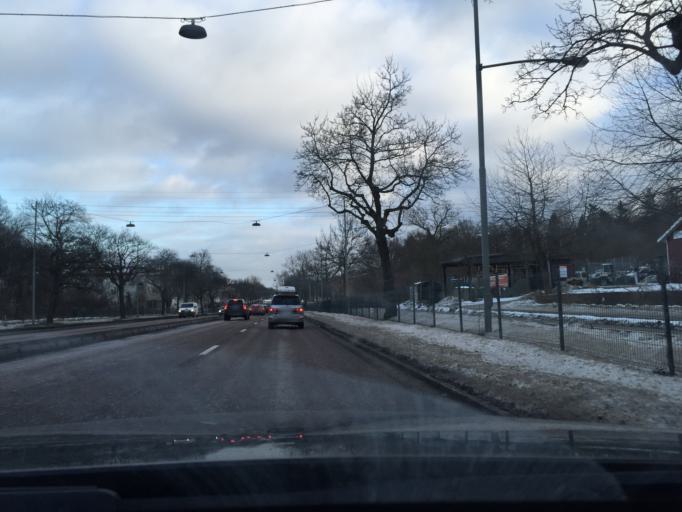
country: SE
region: Stockholm
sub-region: Stockholms Kommun
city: Bromma
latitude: 59.3415
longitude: 17.9303
